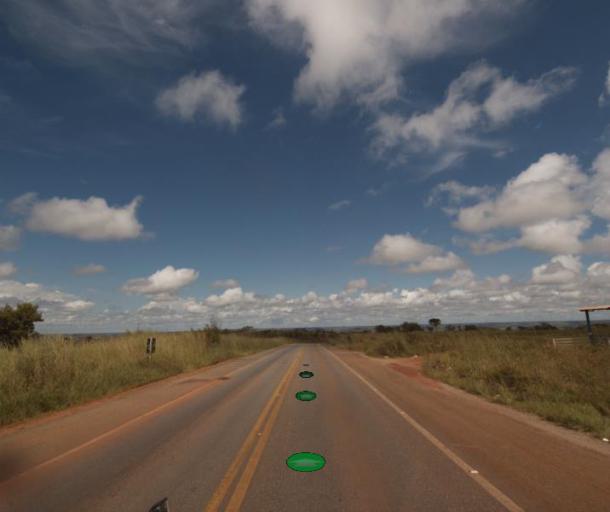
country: BR
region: Federal District
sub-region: Brasilia
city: Brasilia
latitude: -15.7486
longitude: -48.4117
